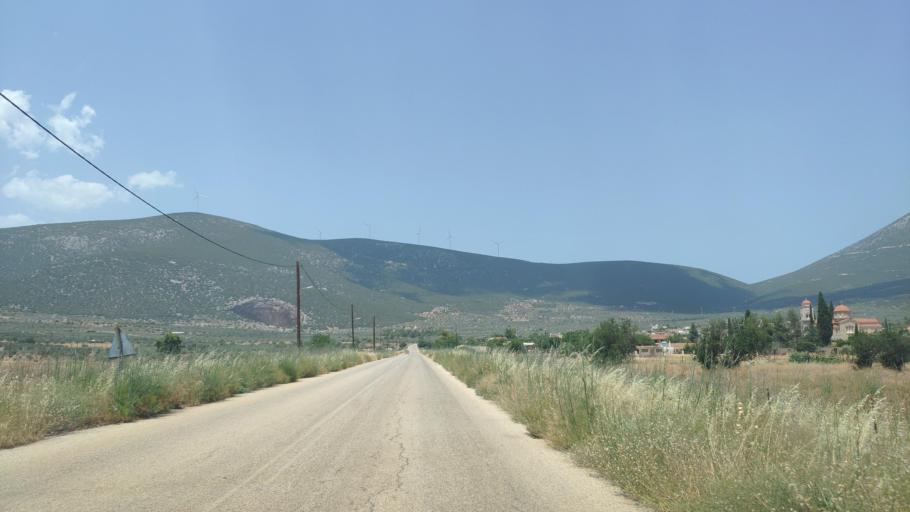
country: GR
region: Peloponnese
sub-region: Nomos Argolidos
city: Didyma
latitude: 37.4579
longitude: 23.1686
